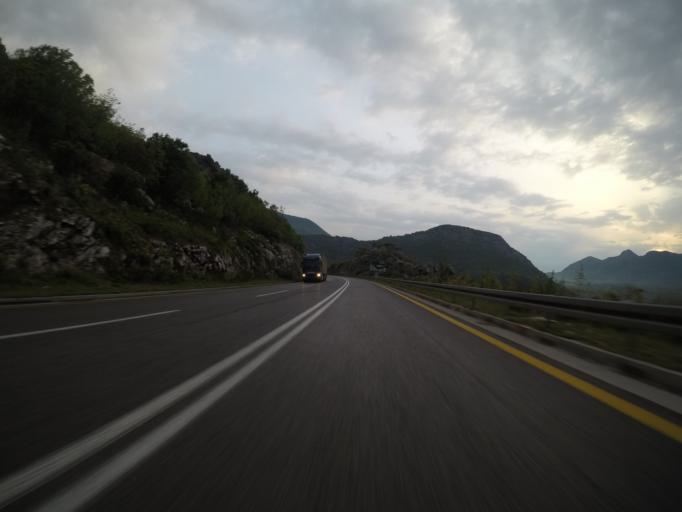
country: ME
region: Bar
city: Sutomore
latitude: 42.2183
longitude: 19.0511
